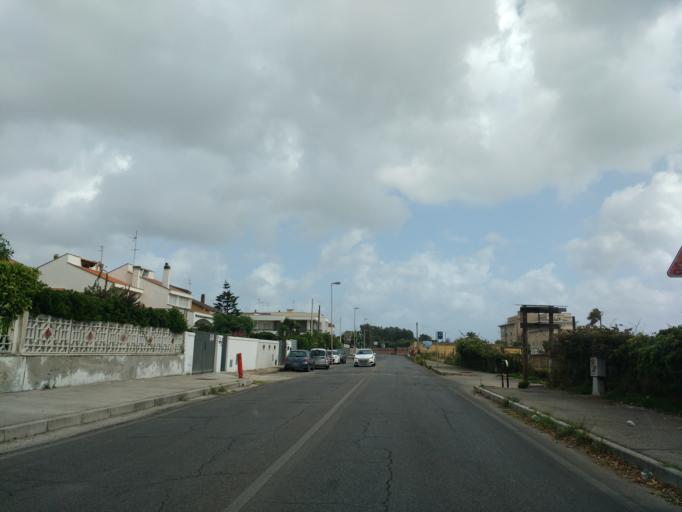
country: IT
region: Latium
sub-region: Citta metropolitana di Roma Capitale
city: Anzio
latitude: 41.4700
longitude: 12.6074
